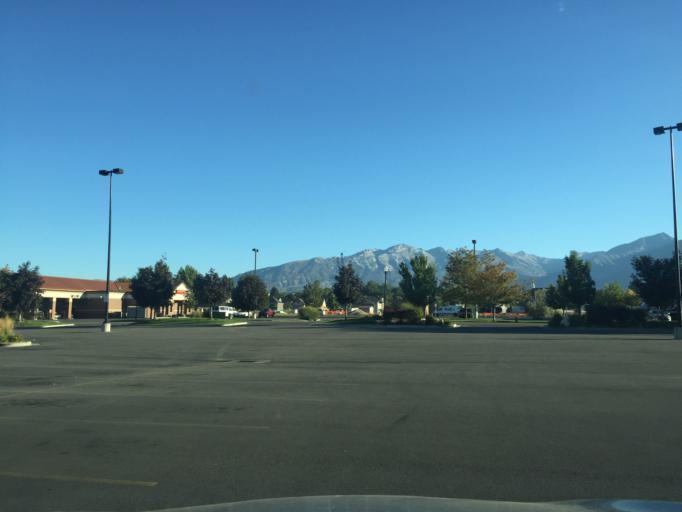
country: US
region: Utah
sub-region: Utah County
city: American Fork
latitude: 40.3846
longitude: -111.8197
